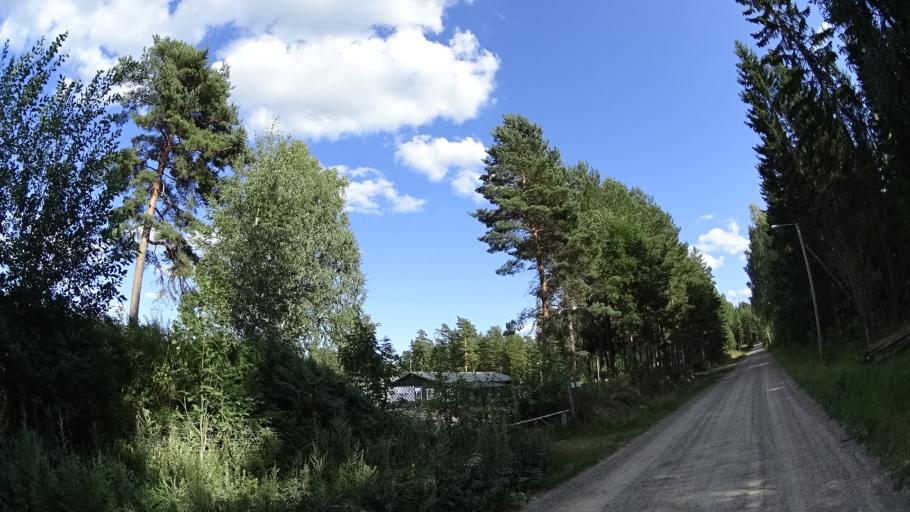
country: FI
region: Uusimaa
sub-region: Helsinki
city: Vihti
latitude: 60.3639
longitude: 24.3524
